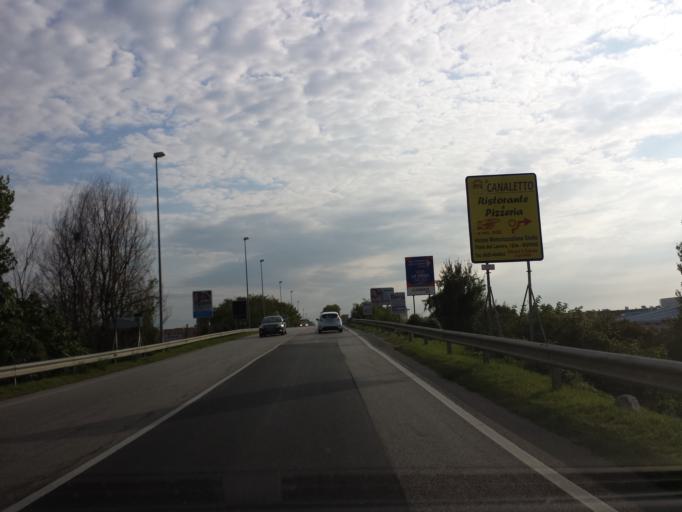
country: IT
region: Veneto
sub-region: Provincia di Rovigo
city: Rovigo
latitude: 45.0558
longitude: 11.7899
